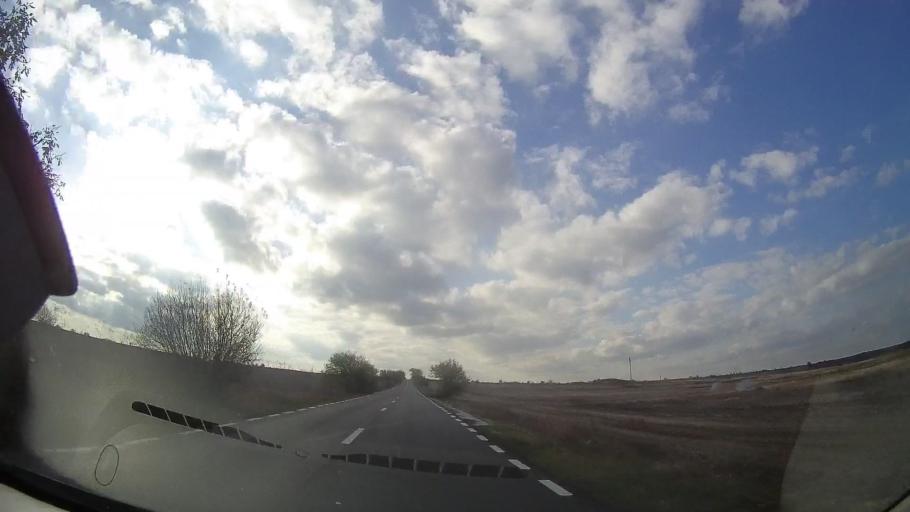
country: RO
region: Constanta
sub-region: Comuna Albesti
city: Albesti
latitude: 43.8147
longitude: 28.4526
